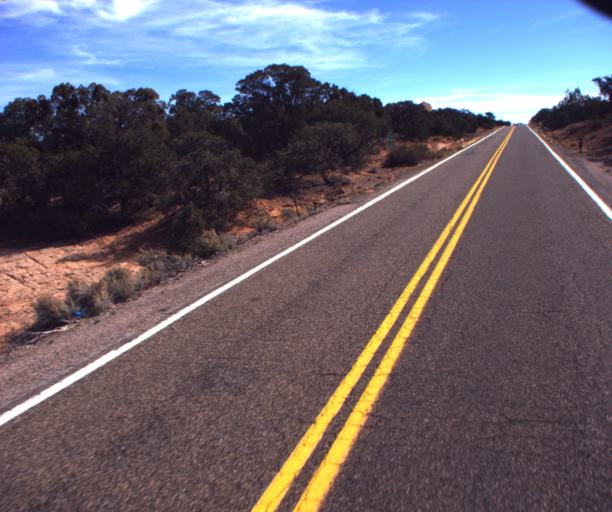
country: US
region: Arizona
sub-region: Navajo County
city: Kayenta
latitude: 36.6699
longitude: -110.5352
